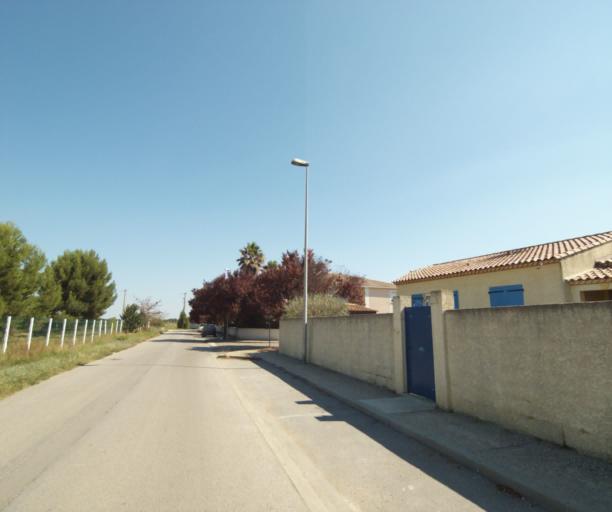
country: FR
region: Languedoc-Roussillon
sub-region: Departement de l'Herault
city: Marsillargues
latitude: 43.6670
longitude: 4.1680
